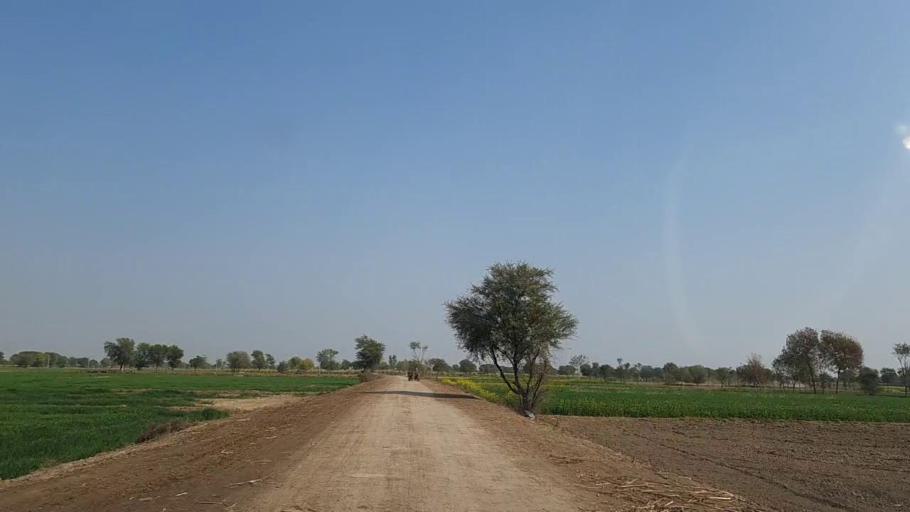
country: PK
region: Sindh
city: Daur
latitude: 26.4303
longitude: 68.2346
